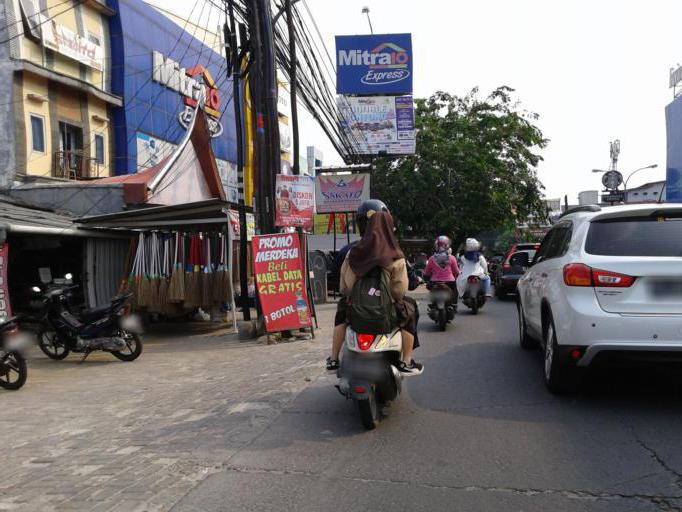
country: ID
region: West Java
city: Pamulang
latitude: -6.3324
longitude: 106.7833
